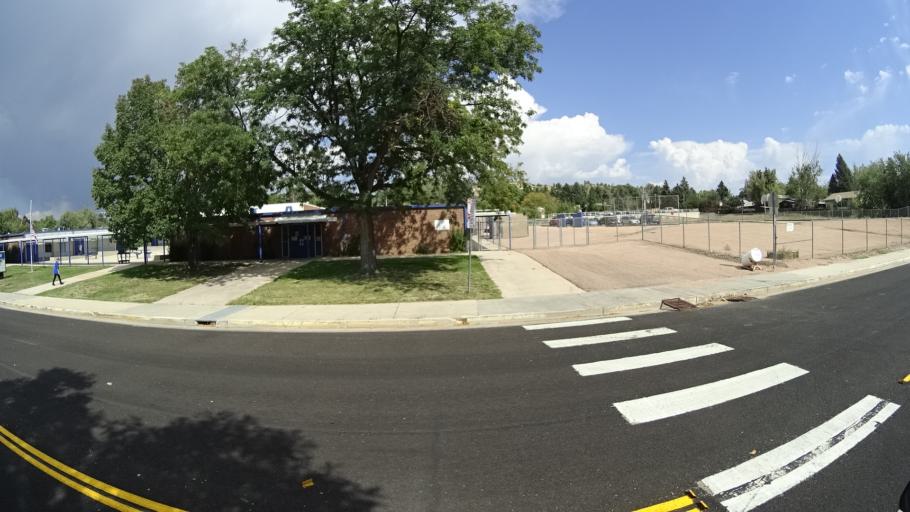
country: US
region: Colorado
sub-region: El Paso County
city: Colorado Springs
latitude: 38.8641
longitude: -104.7675
